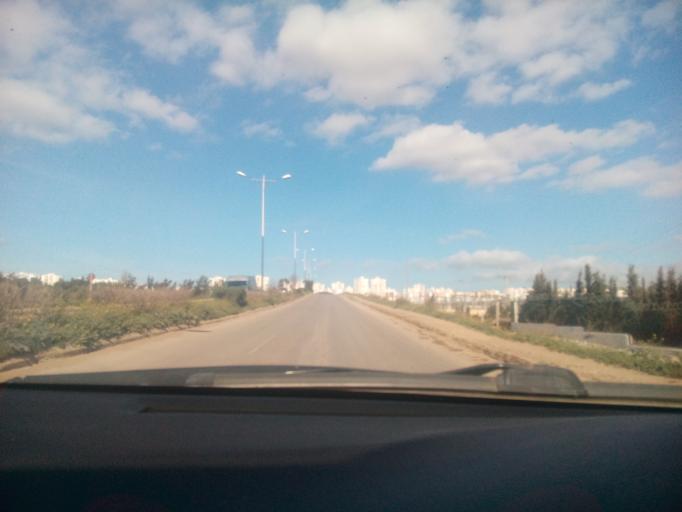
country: DZ
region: Oran
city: Bir el Djir
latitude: 35.6900
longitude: -0.5755
